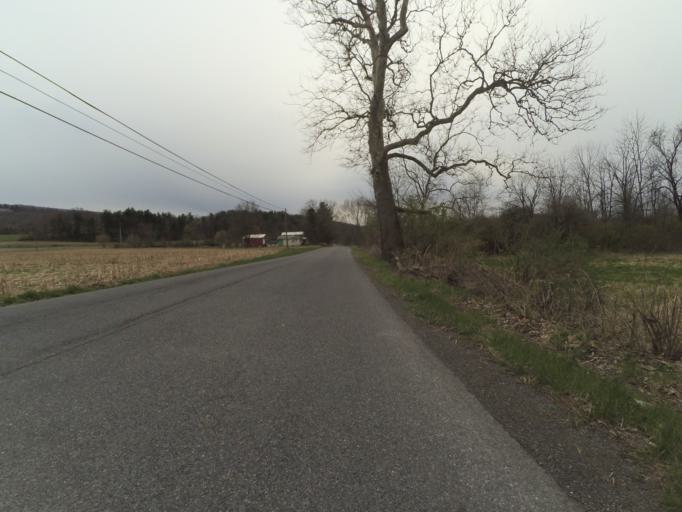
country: US
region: Pennsylvania
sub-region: Centre County
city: Milesburg
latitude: 40.9701
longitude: -77.7400
